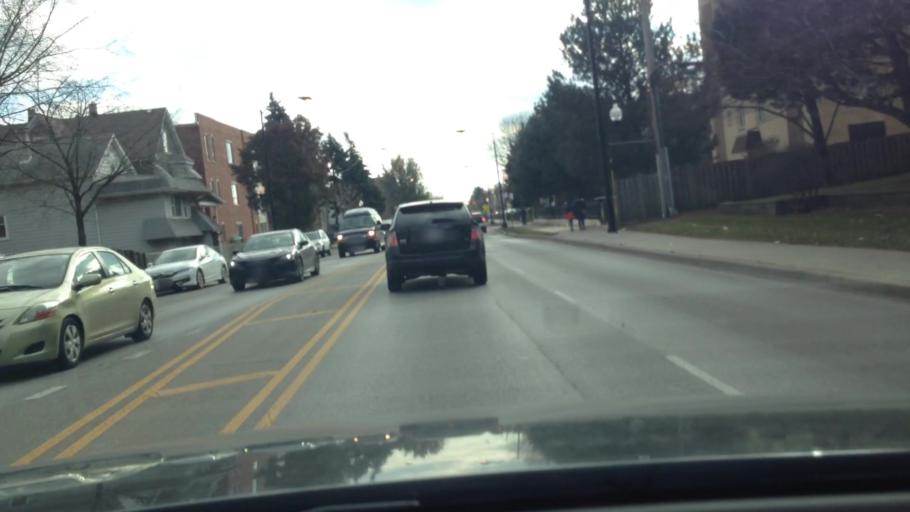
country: US
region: Illinois
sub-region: Cook County
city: Harwood Heights
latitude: 41.9560
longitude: -87.7867
